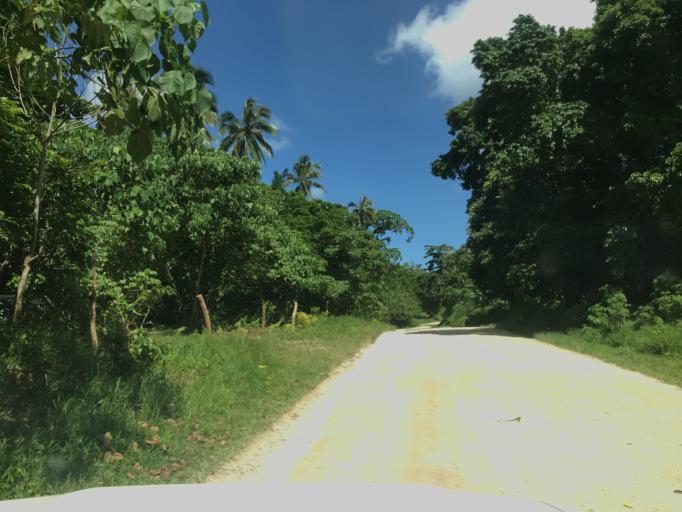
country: VU
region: Sanma
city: Luganville
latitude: -15.5783
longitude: 167.0367
